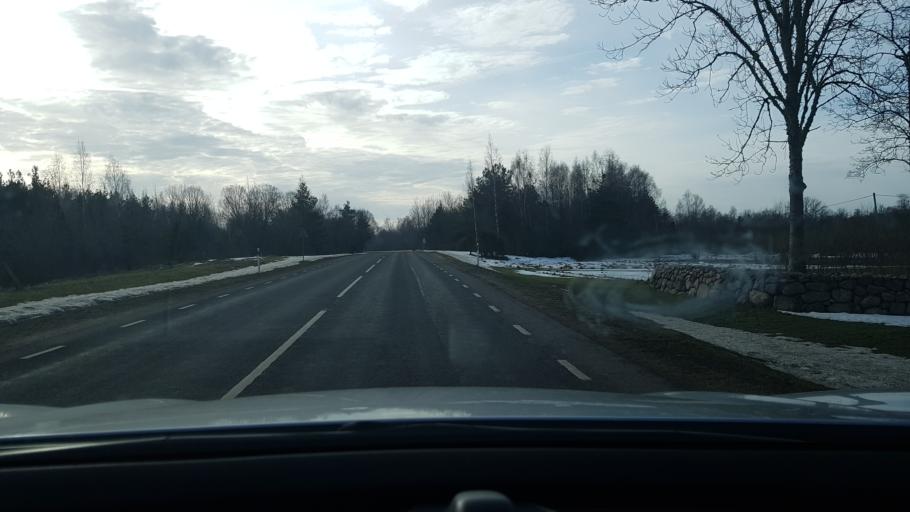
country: EE
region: Saare
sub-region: Kuressaare linn
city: Kuressaare
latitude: 58.3073
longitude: 22.5407
